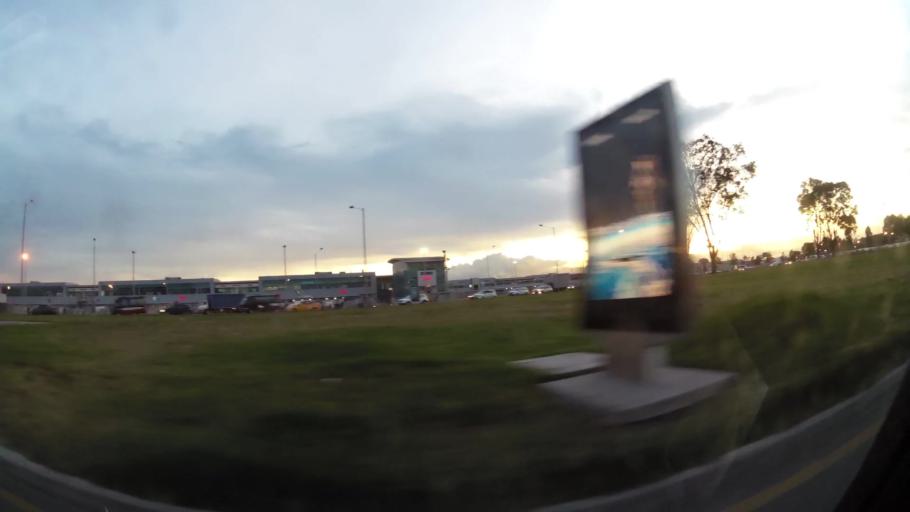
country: CO
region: Cundinamarca
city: Funza
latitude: 4.6943
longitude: -74.1370
